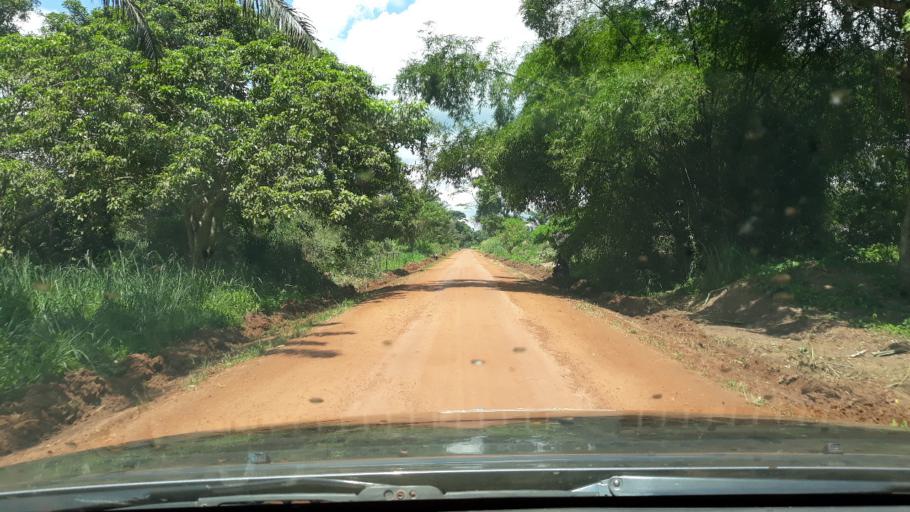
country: CD
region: Equateur
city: Gemena
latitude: 2.5911
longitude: 20.0422
